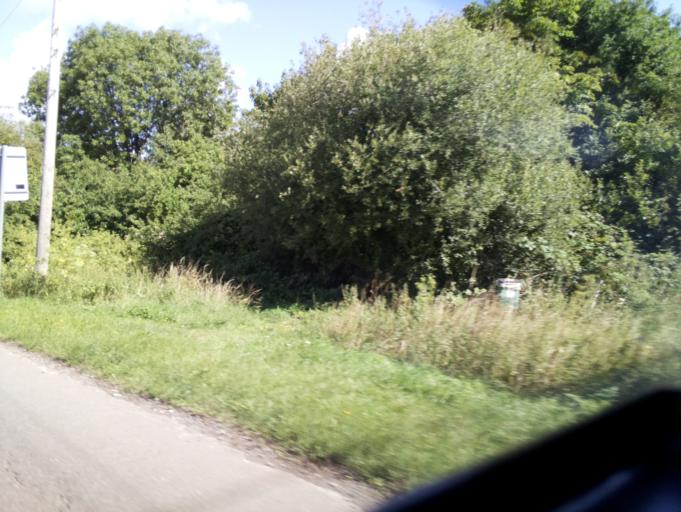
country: GB
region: England
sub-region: Gloucestershire
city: Newent
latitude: 51.9078
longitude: -2.3367
